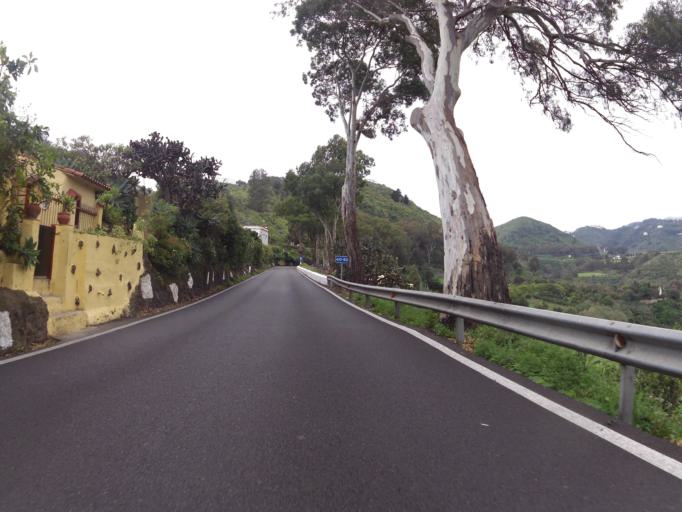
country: ES
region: Canary Islands
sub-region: Provincia de Las Palmas
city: Teror
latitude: 28.0789
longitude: -15.5186
